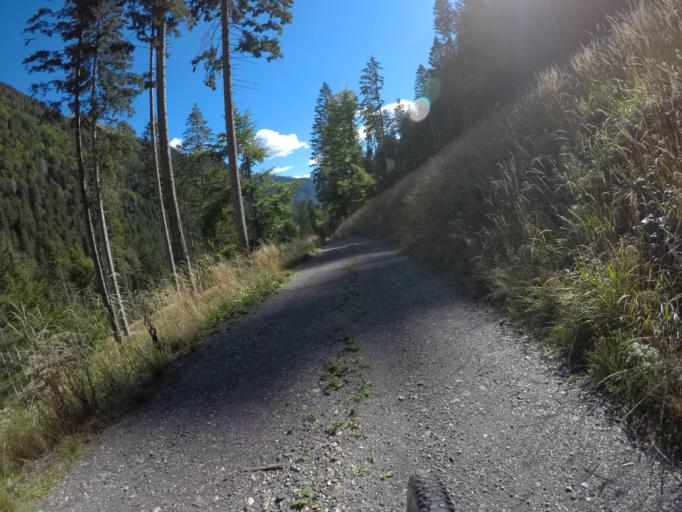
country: IT
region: Friuli Venezia Giulia
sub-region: Provincia di Udine
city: Ligosullo
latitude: 46.5824
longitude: 13.0894
